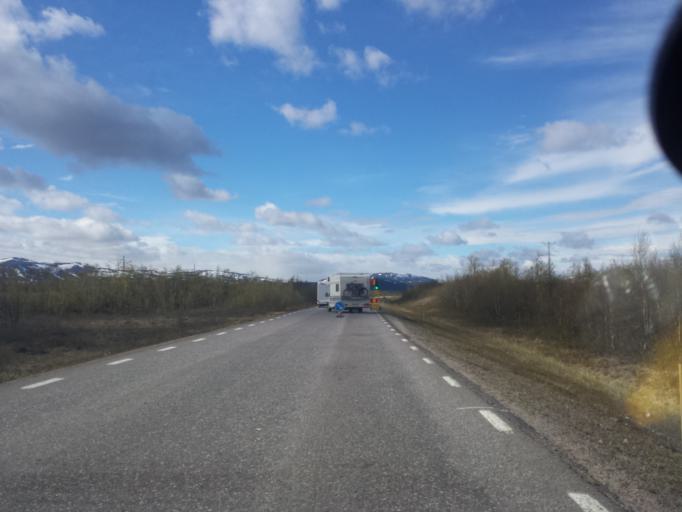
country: SE
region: Norrbotten
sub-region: Kiruna Kommun
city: Kiruna
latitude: 68.0048
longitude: 19.8523
